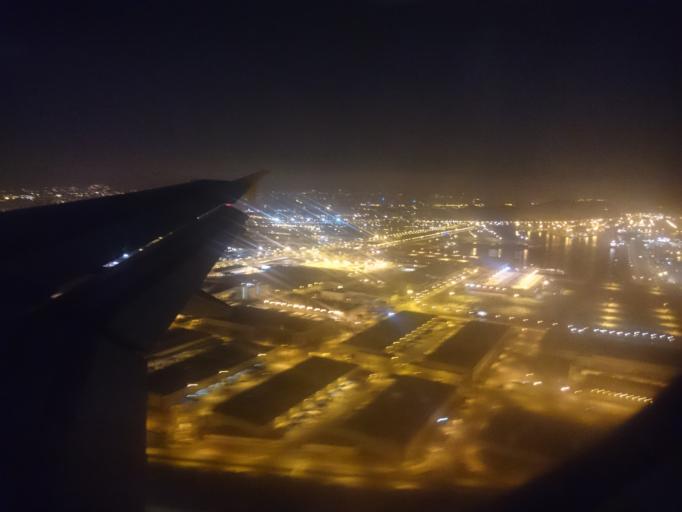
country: ES
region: Catalonia
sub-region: Provincia de Barcelona
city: El Prat de Llobregat
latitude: 41.3189
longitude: 2.1417
